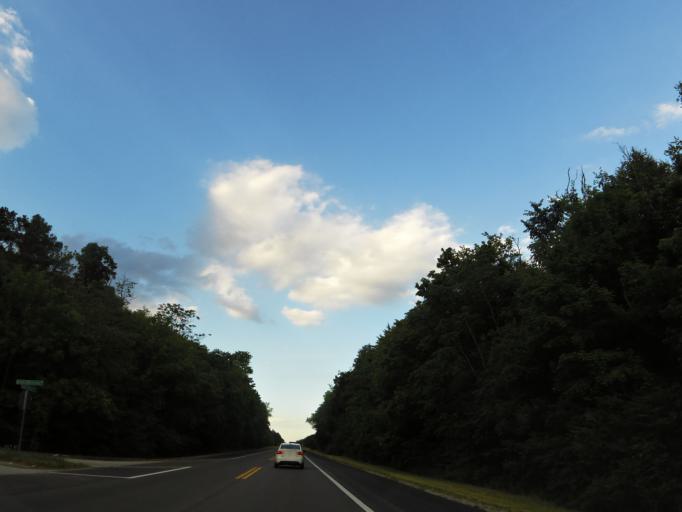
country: US
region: Tennessee
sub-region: Maury County
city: Spring Hill
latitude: 35.6388
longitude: -86.9129
